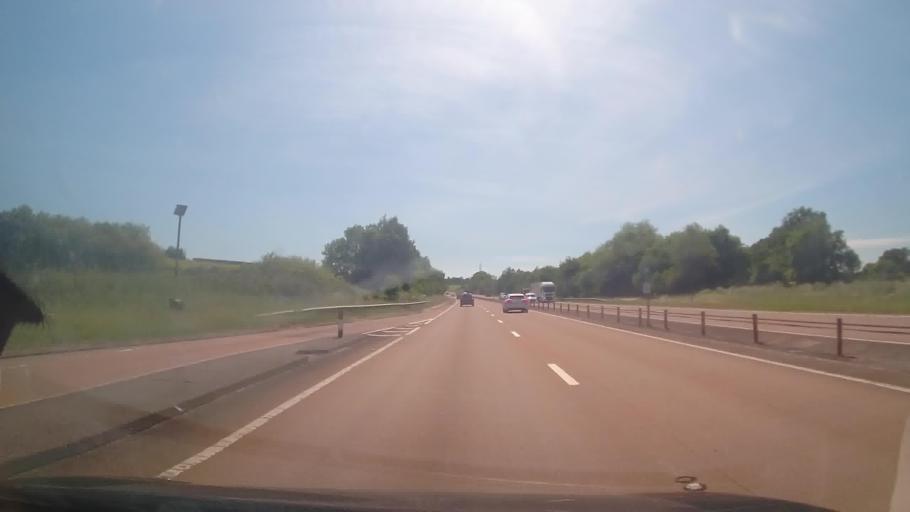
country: GB
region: England
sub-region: Devon
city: Newton Poppleford
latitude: 50.7440
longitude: -3.3581
